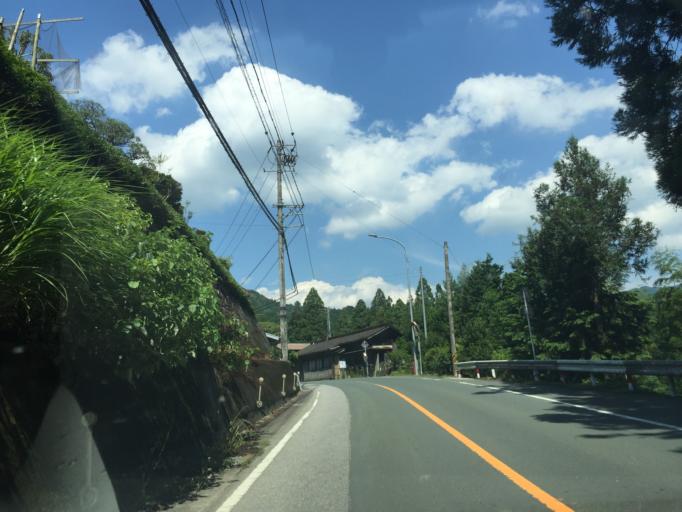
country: JP
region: Shizuoka
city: Hamakita
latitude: 35.0361
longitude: 137.7160
